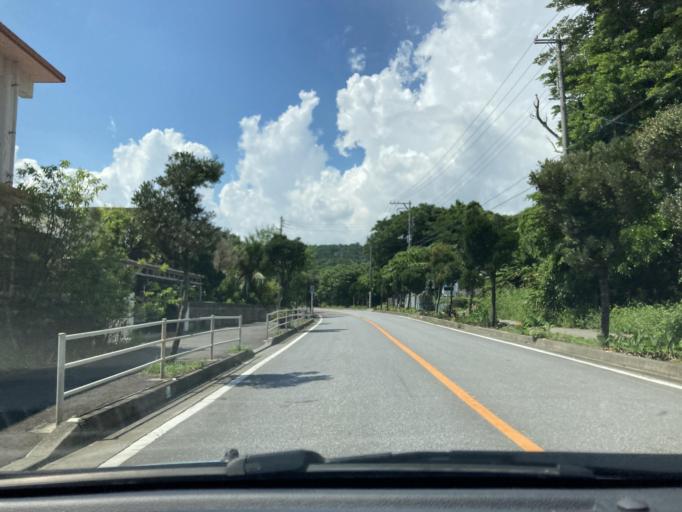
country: JP
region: Okinawa
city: Ginowan
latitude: 26.1822
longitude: 127.7712
